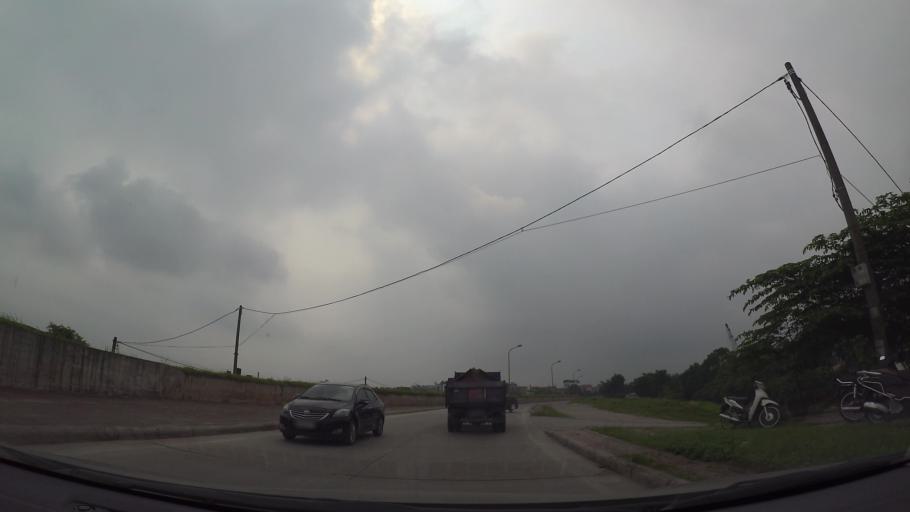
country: VN
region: Ha Noi
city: Trau Quy
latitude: 21.0755
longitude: 105.9139
